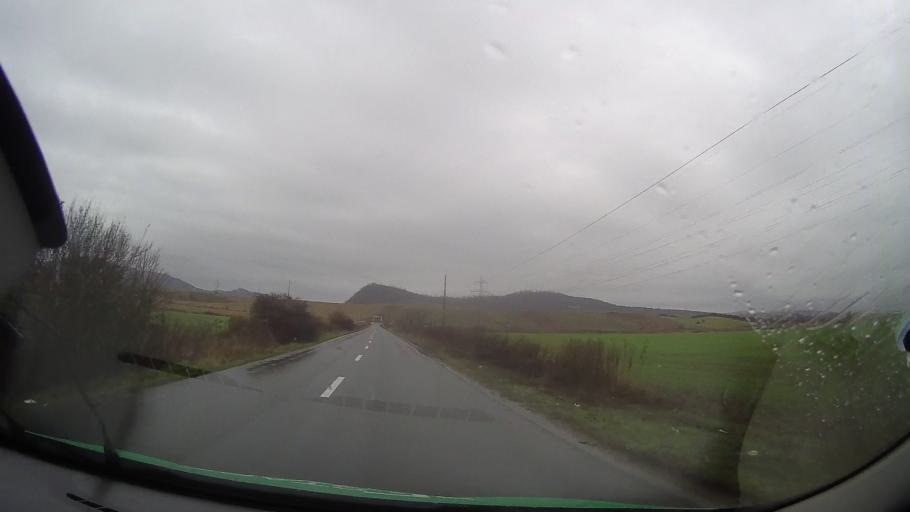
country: RO
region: Bistrita-Nasaud
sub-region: Municipiul Bistrita
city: Viisoara
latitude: 47.0531
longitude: 24.4504
